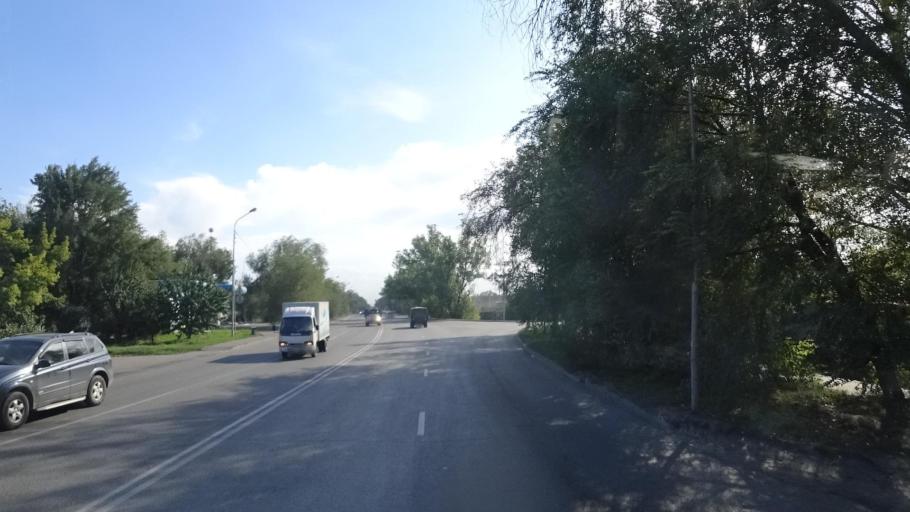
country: KZ
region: Almaty Oblysy
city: Energeticheskiy
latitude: 43.3795
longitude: 76.9967
